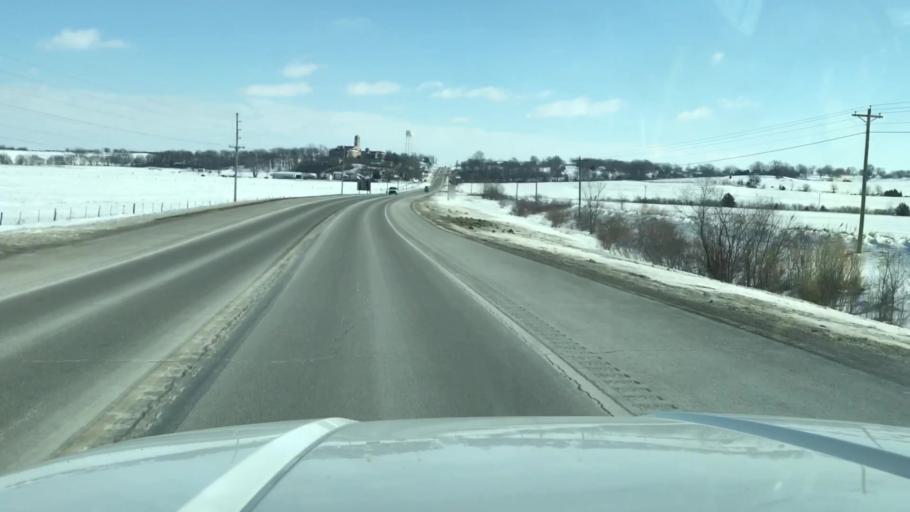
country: US
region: Missouri
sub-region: Nodaway County
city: Maryville
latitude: 40.3449
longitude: -94.8285
